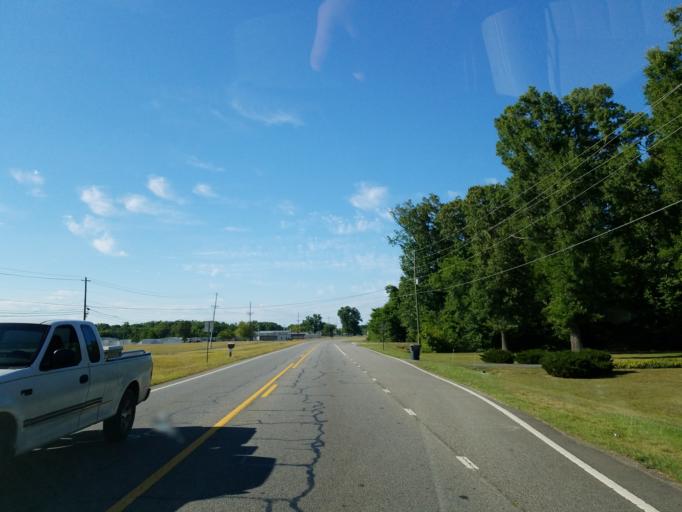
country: US
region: Georgia
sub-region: Gordon County
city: Calhoun
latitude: 34.4526
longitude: -84.9354
